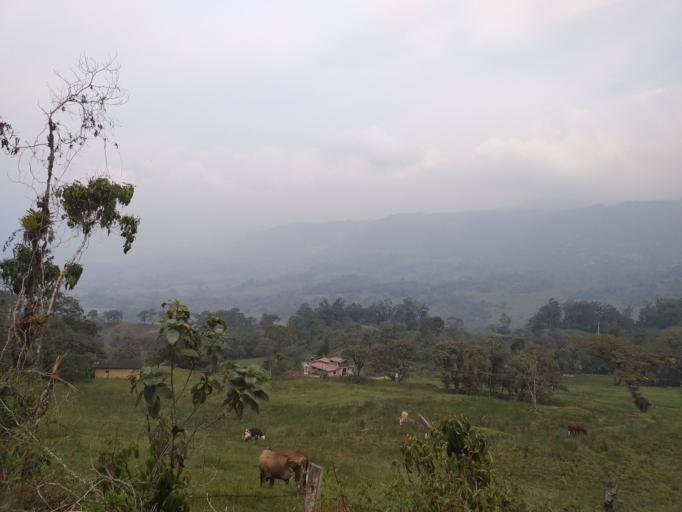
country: CO
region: Boyaca
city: Aquitania
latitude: 5.3075
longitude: -72.9484
